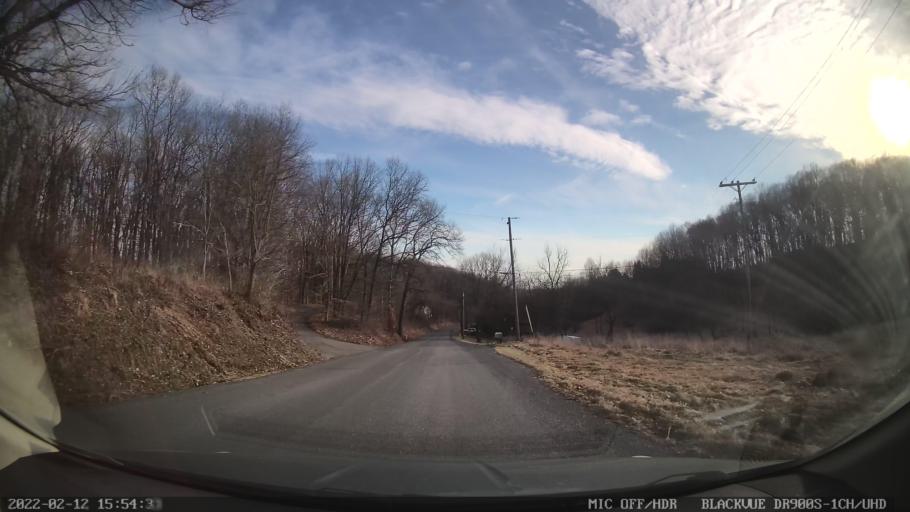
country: US
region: Pennsylvania
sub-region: Berks County
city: Kutztown
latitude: 40.5703
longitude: -75.7516
